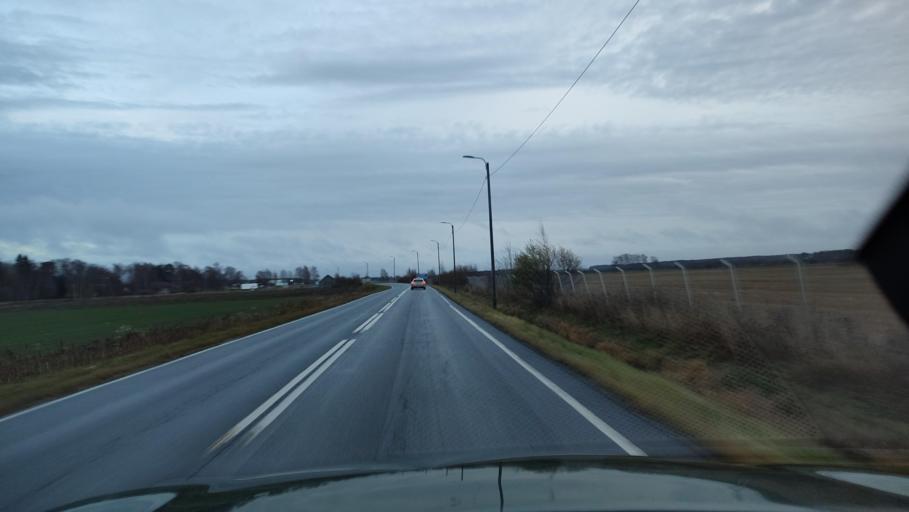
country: FI
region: Ostrobothnia
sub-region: Vaasa
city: Ristinummi
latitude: 63.0452
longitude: 21.7479
